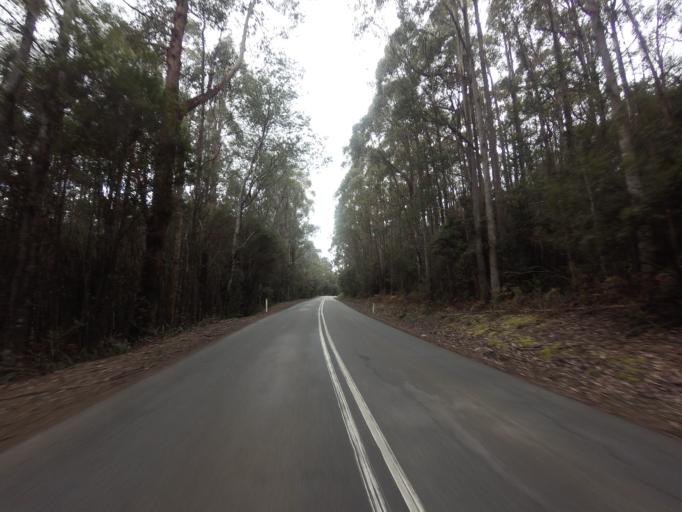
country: AU
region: Tasmania
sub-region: Huon Valley
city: Geeveston
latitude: -43.3926
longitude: 146.9569
